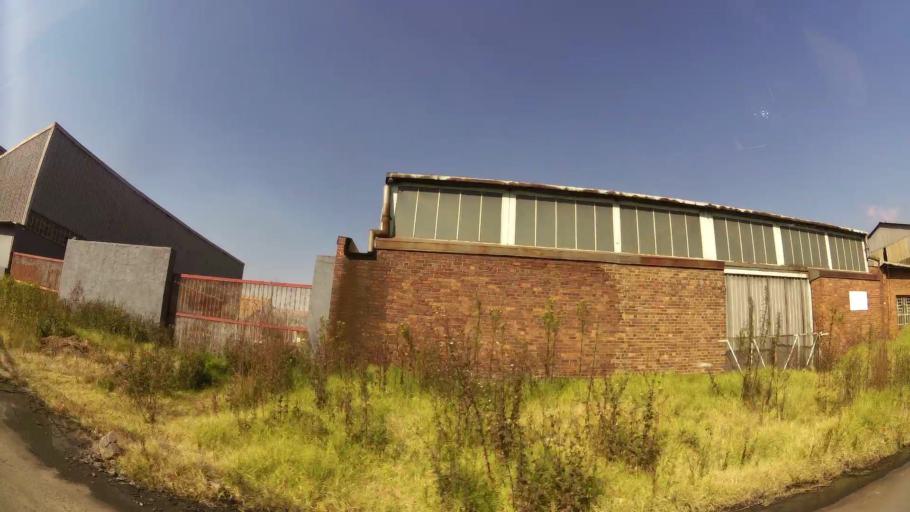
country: ZA
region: Gauteng
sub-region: Ekurhuleni Metropolitan Municipality
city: Benoni
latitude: -26.2040
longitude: 28.3070
